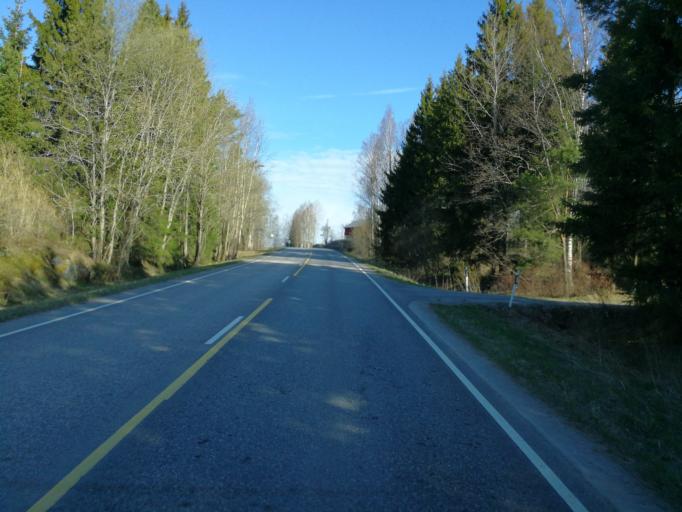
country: FI
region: Uusimaa
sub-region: Helsinki
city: Espoo
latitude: 60.1982
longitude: 24.5569
